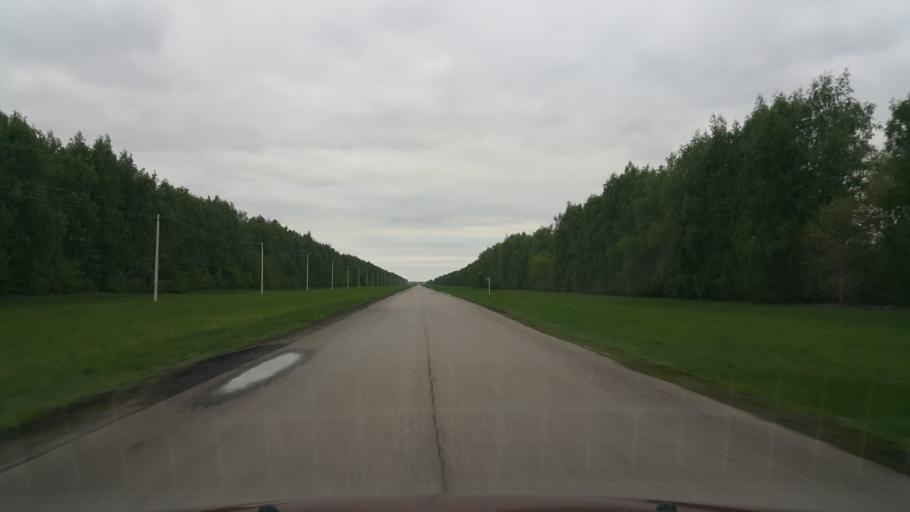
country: RU
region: Tambov
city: Znamenka
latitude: 52.3726
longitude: 41.2841
